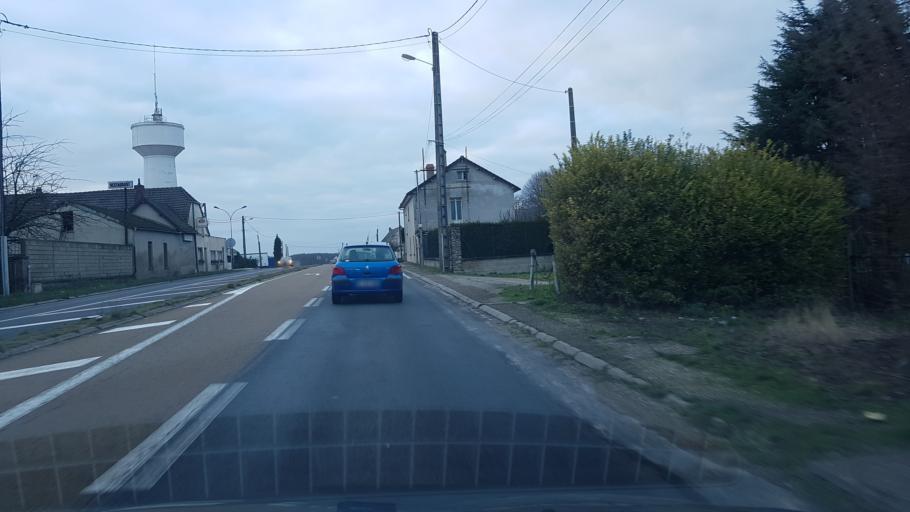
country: FR
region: Champagne-Ardenne
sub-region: Departement de la Marne
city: Esternay
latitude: 48.7318
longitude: 3.6122
